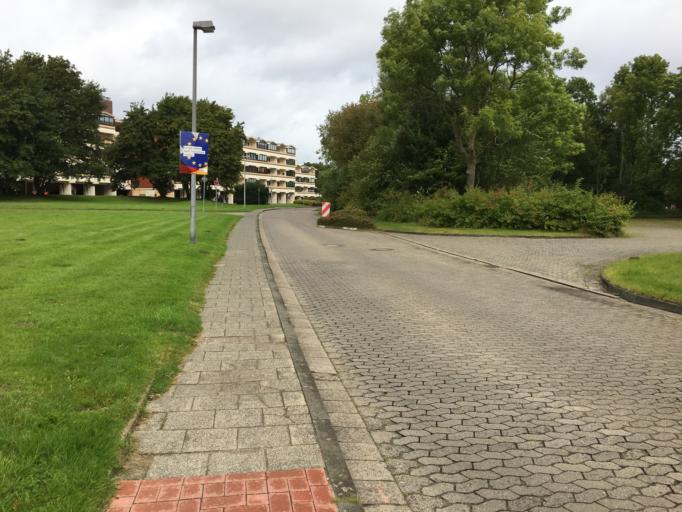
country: DE
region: Schleswig-Holstein
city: Wisch
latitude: 54.4195
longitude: 10.3702
